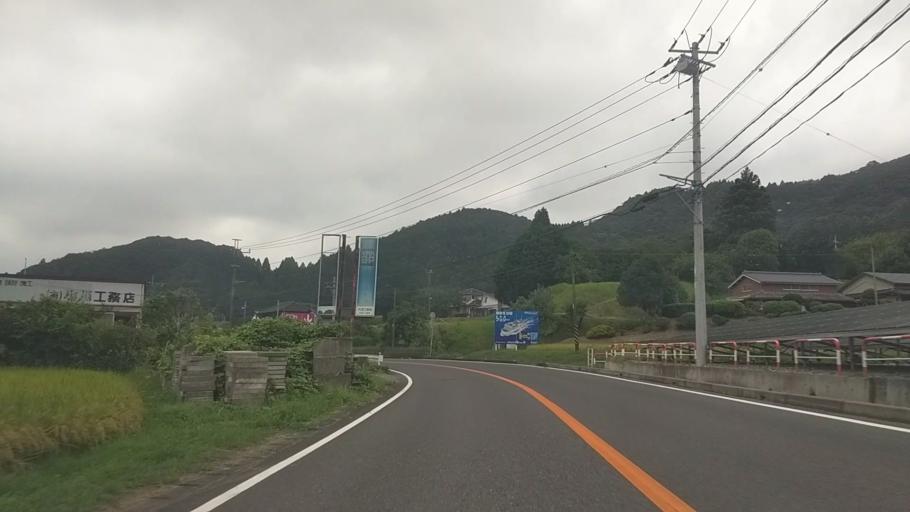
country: JP
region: Chiba
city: Kawaguchi
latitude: 35.1427
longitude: 139.9723
